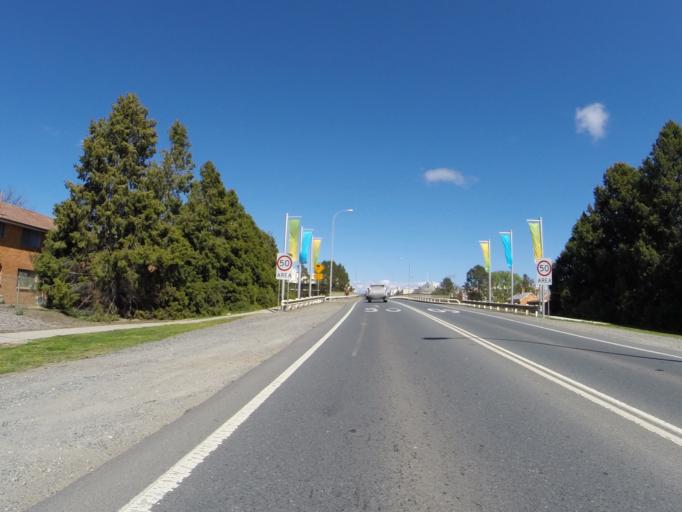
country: AU
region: New South Wales
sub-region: Queanbeyan
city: Queanbeyan
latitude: -35.3514
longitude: 149.2385
